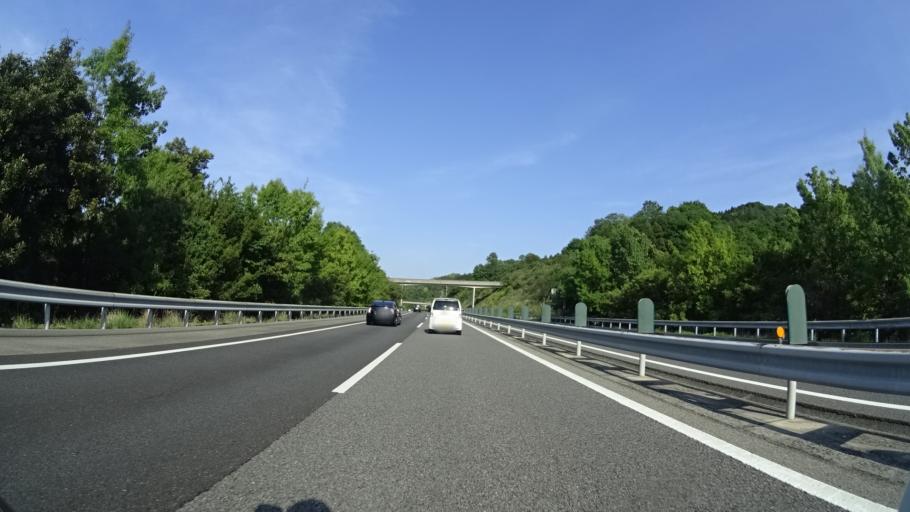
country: JP
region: Ehime
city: Saijo
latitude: 33.8826
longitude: 133.1175
